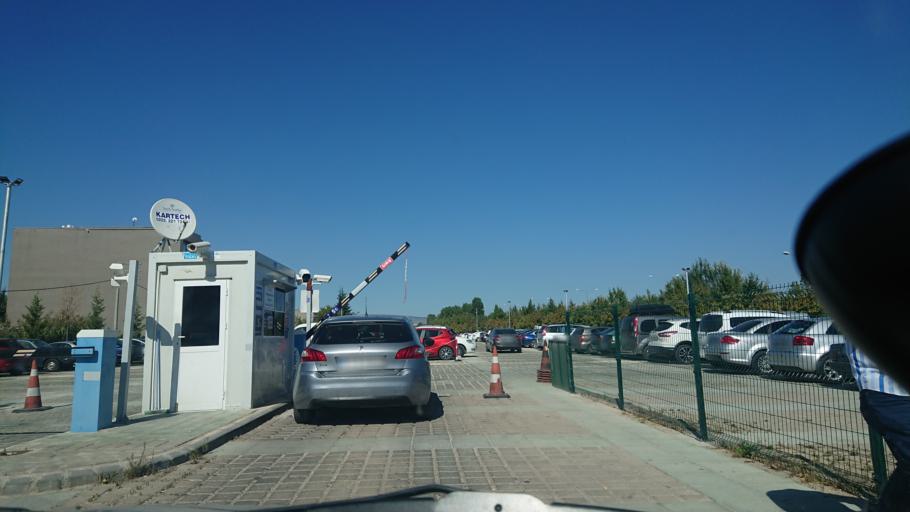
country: TR
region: Eskisehir
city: Eskisehir
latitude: 39.7656
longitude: 30.4708
